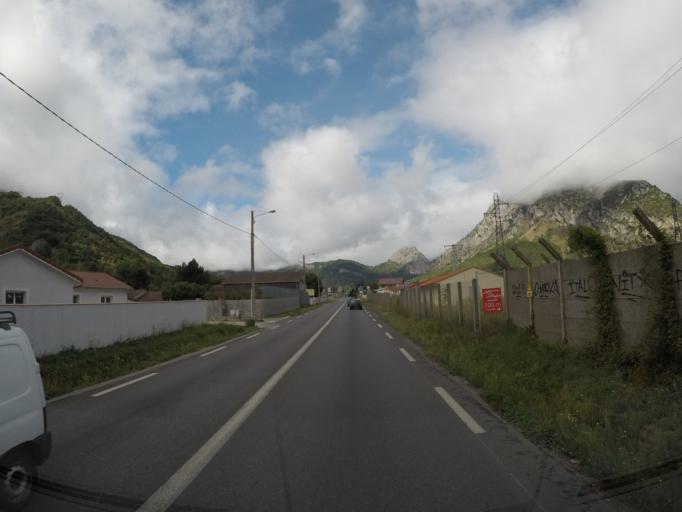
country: FR
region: Midi-Pyrenees
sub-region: Departement de l'Ariege
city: Tarascon-sur-Ariege
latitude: 42.8508
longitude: 1.5971
